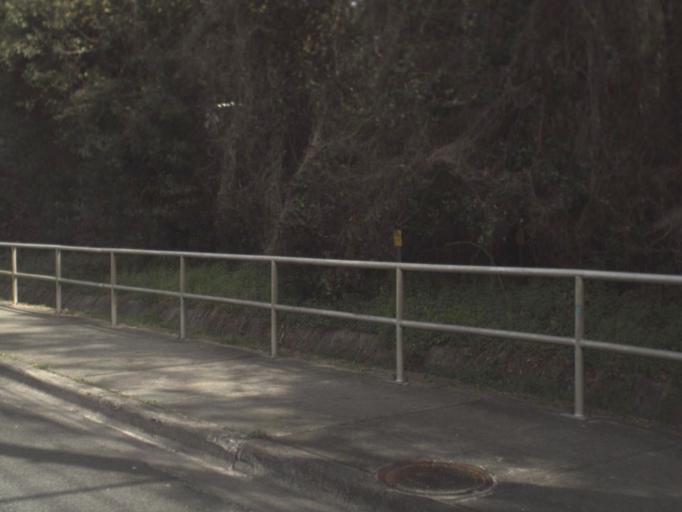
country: US
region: Florida
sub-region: Leon County
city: Tallahassee
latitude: 30.5219
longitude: -84.2384
